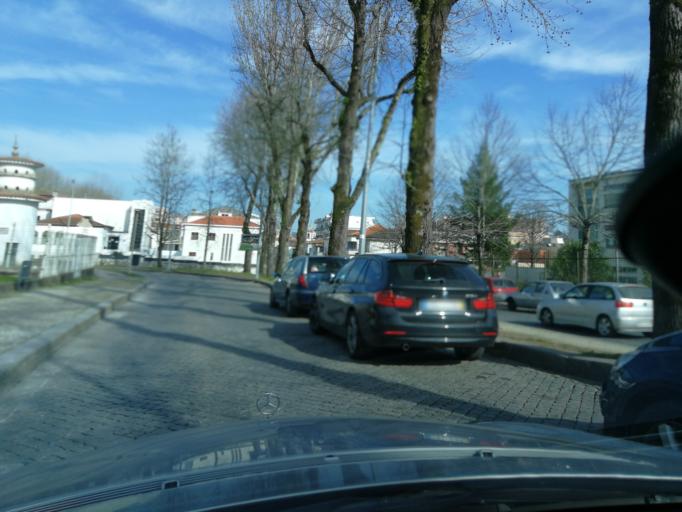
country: PT
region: Braga
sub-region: Vila Nova de Famalicao
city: Vila Nova de Famalicao
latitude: 41.4065
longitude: -8.5244
